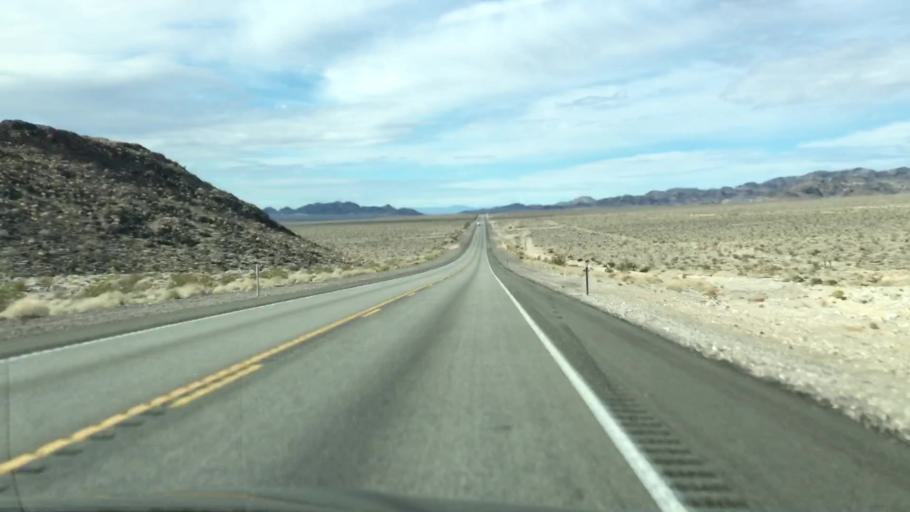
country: US
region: Nevada
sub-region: Nye County
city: Pahrump
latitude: 36.5828
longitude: -116.2066
